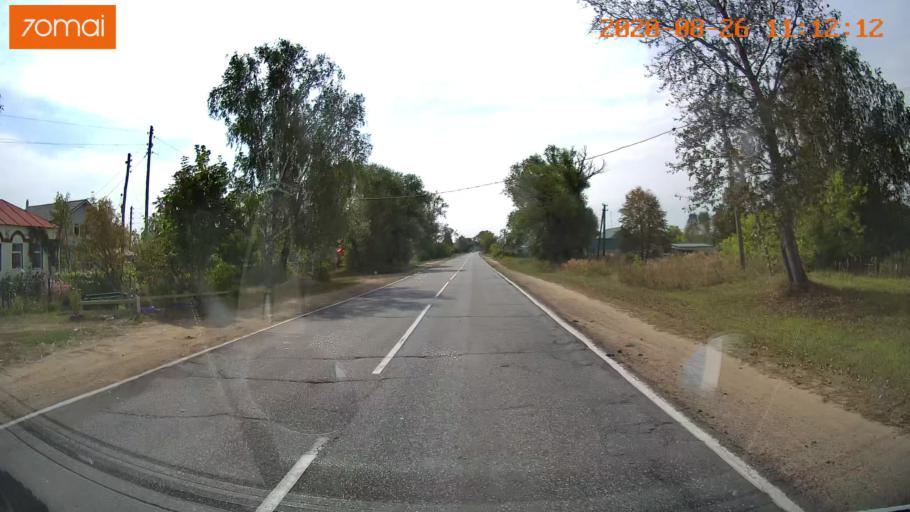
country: RU
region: Rjazan
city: Izhevskoye
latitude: 54.4729
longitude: 41.1255
